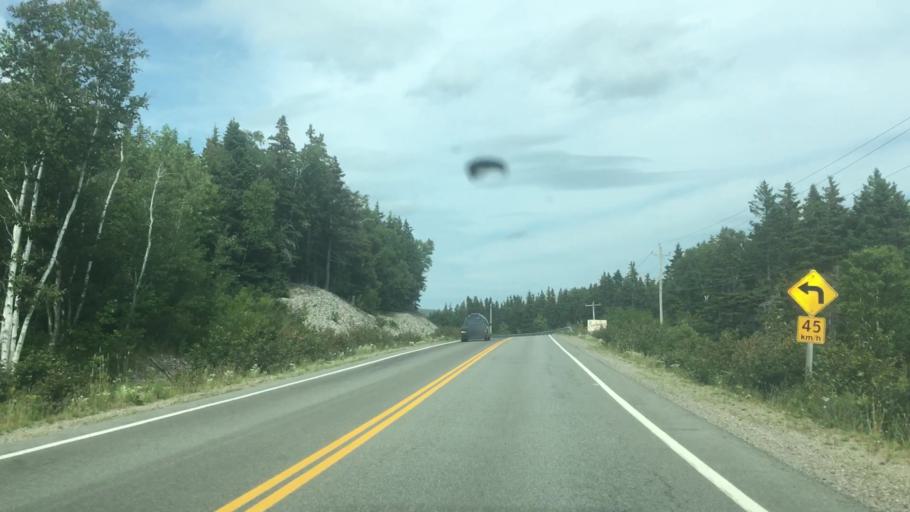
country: CA
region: Nova Scotia
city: Sydney Mines
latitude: 46.5358
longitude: -60.4141
